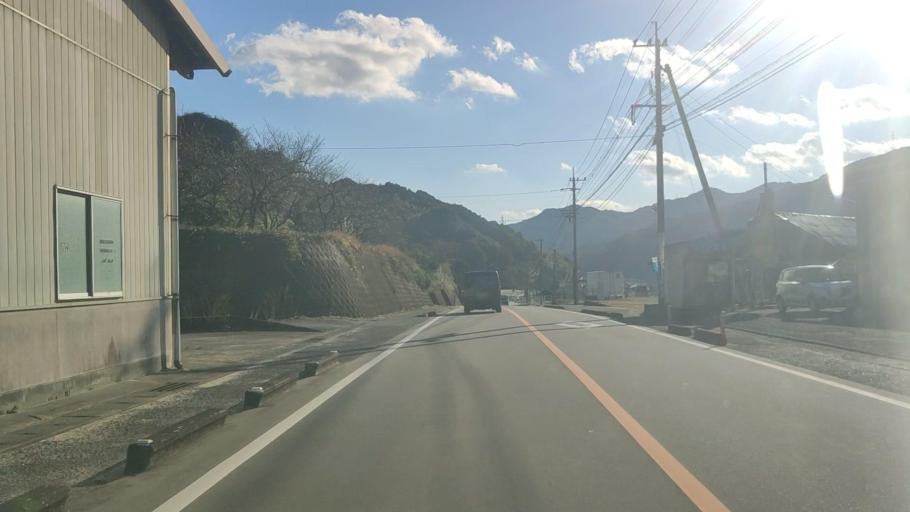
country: JP
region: Saga Prefecture
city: Saga-shi
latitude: 33.3623
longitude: 130.2541
